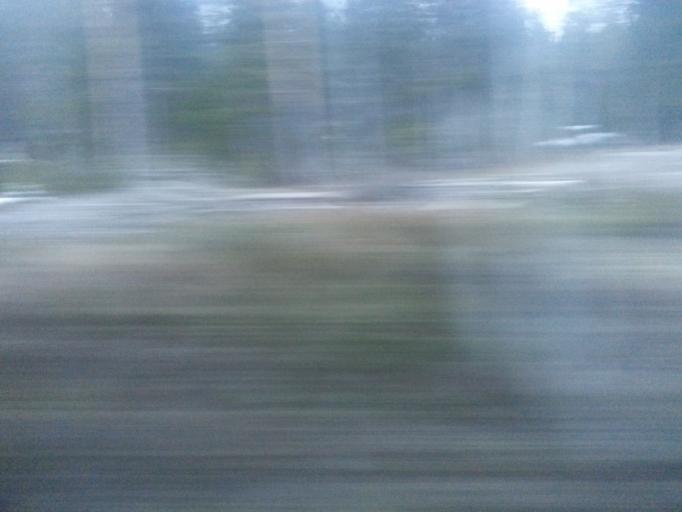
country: NO
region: Sor-Trondelag
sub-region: Rennebu
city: Berkak
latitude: 62.7826
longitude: 9.9938
